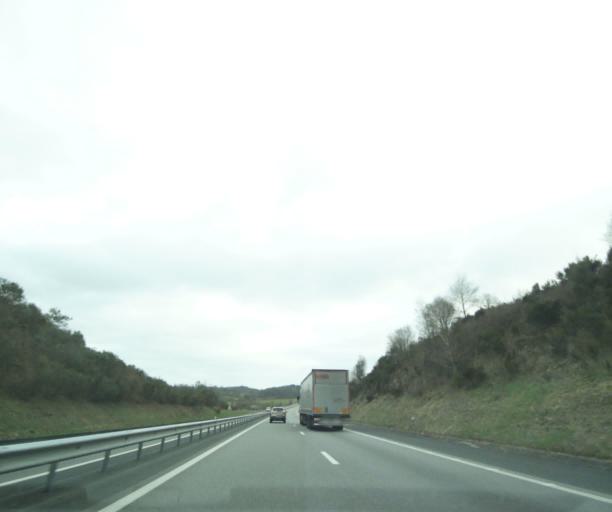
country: FR
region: Limousin
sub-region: Departement de la Correze
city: Vigeois
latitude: 45.3417
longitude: 1.5718
